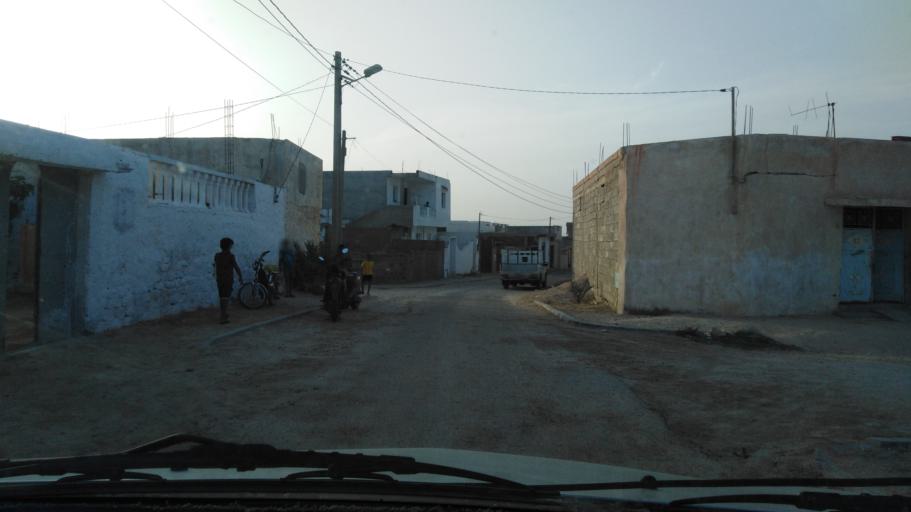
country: TN
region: Qabis
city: Gabes
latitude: 33.9521
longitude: 9.9967
